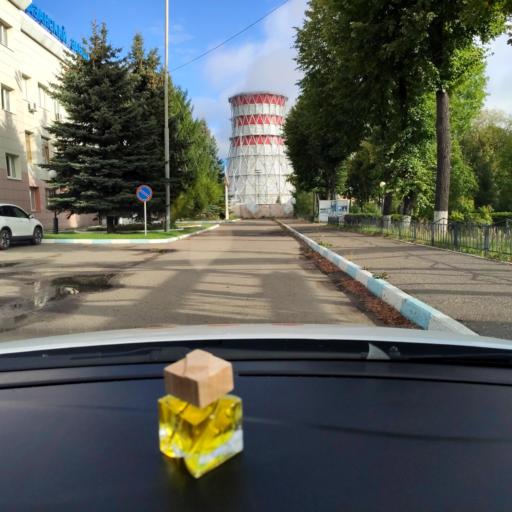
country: RU
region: Tatarstan
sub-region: Gorod Kazan'
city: Kazan
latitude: 55.7557
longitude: 49.1221
